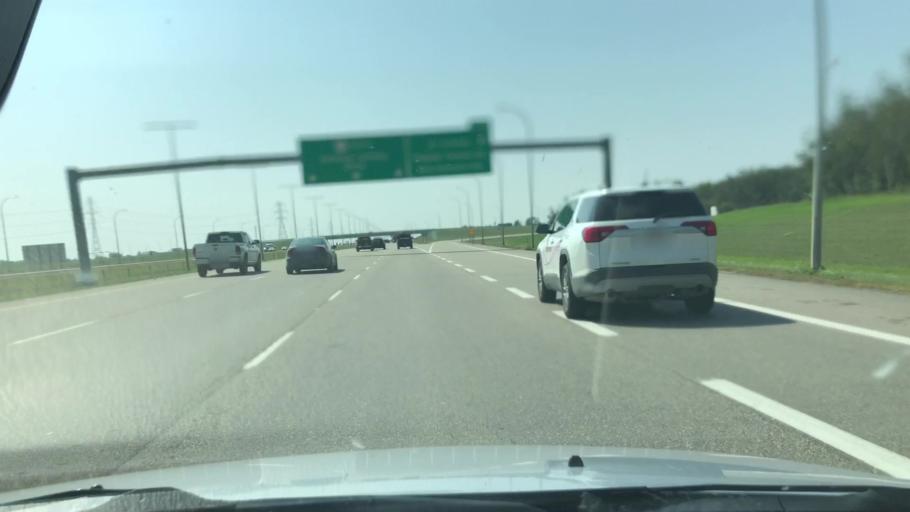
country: CA
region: Alberta
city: St. Albert
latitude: 53.5293
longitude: -113.6593
